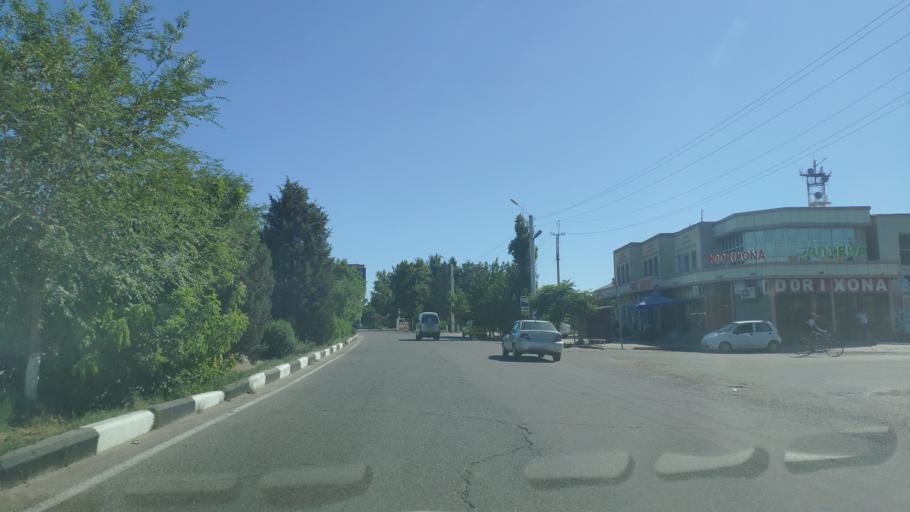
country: UZ
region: Bukhara
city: Bukhara
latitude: 39.7934
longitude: 64.4201
